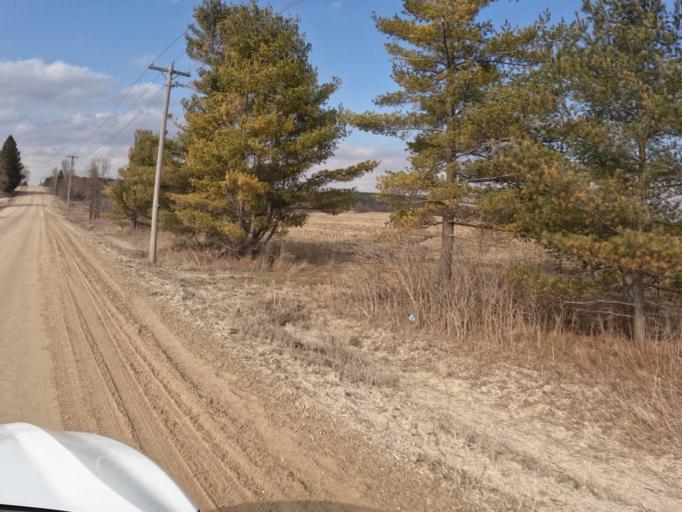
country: CA
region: Ontario
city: Orangeville
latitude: 43.8965
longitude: -80.3004
